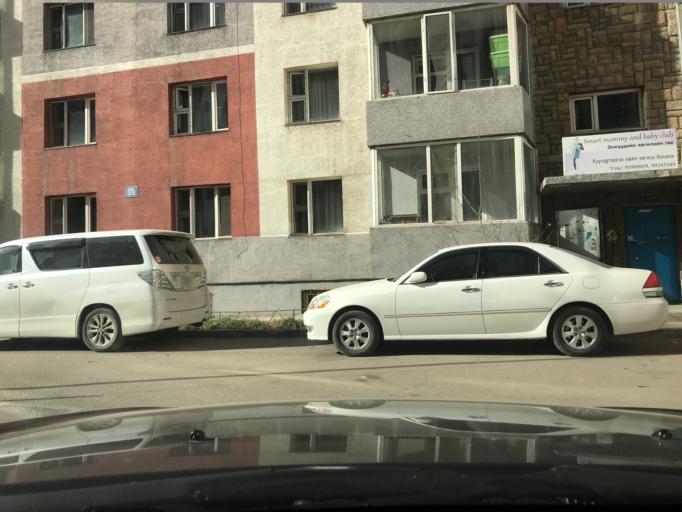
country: MN
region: Ulaanbaatar
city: Ulaanbaatar
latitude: 47.9105
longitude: 106.9406
